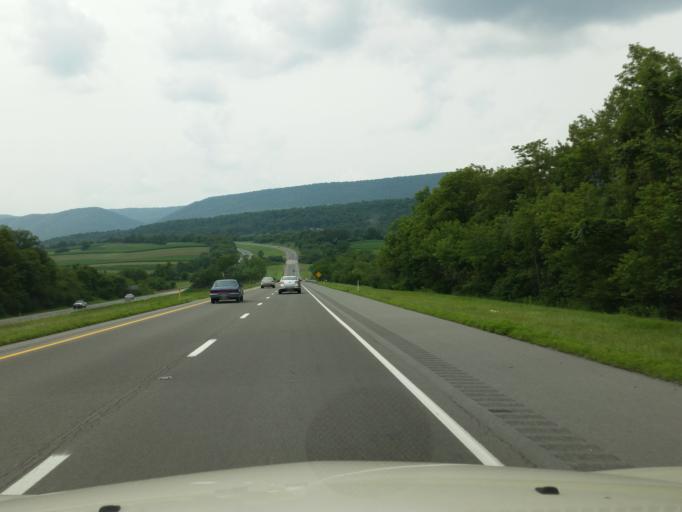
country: US
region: Pennsylvania
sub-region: Juniata County
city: Mifflintown
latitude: 40.5991
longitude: -77.3859
